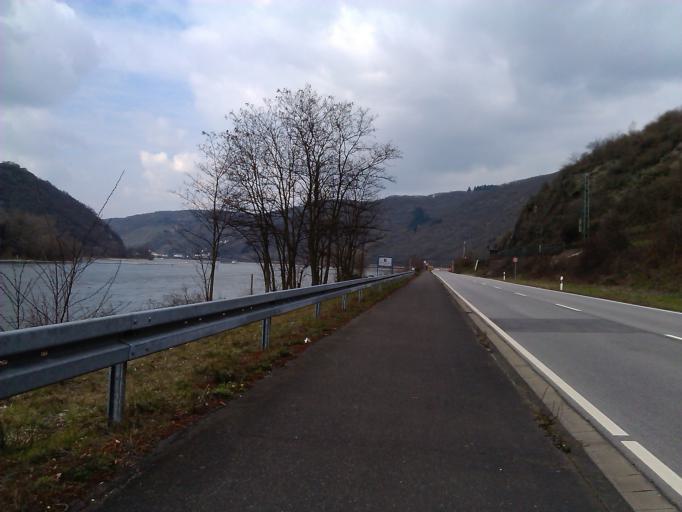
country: DE
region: Rheinland-Pfalz
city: Bacharach
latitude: 50.0642
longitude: 7.7765
